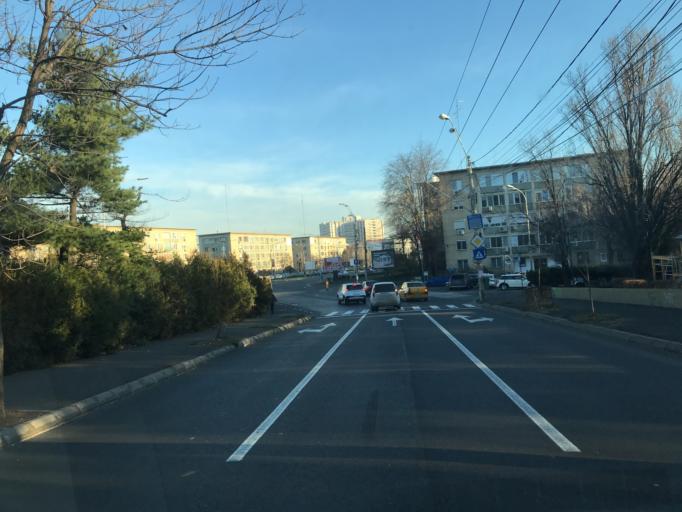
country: RO
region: Bucuresti
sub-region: Municipiul Bucuresti
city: Bucuresti
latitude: 44.4303
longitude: 26.0679
